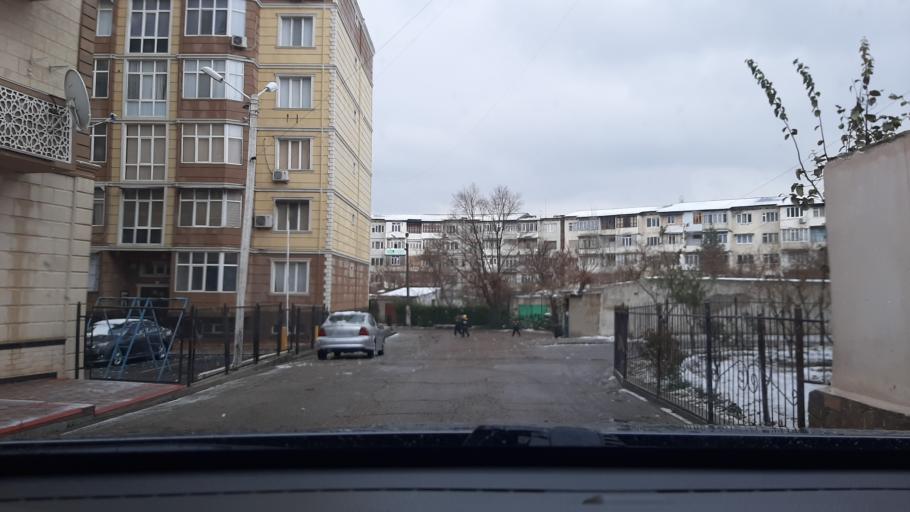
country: TJ
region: Viloyati Sughd
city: Khujand
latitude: 40.3008
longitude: 69.6079
